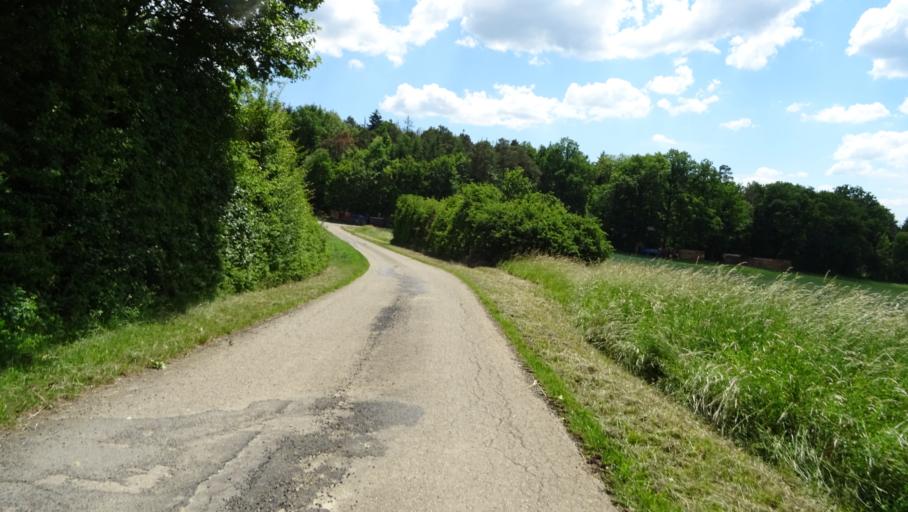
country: DE
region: Baden-Wuerttemberg
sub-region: Karlsruhe Region
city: Adelsheim
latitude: 49.4234
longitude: 9.3654
